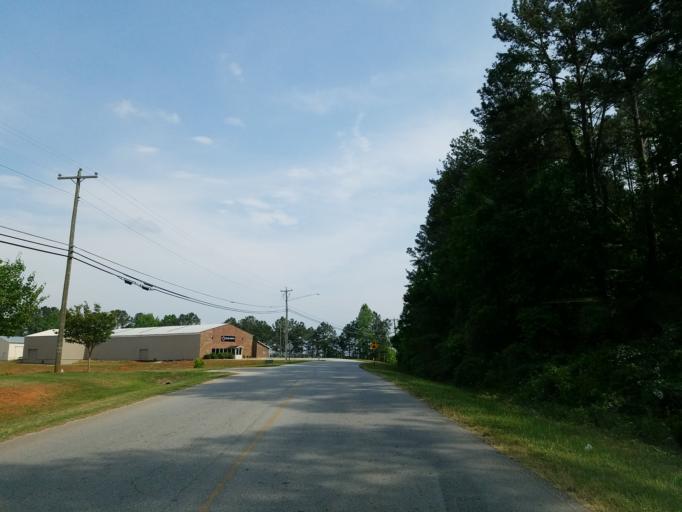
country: US
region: Georgia
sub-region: Paulding County
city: Dallas
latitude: 33.9062
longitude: -84.8028
